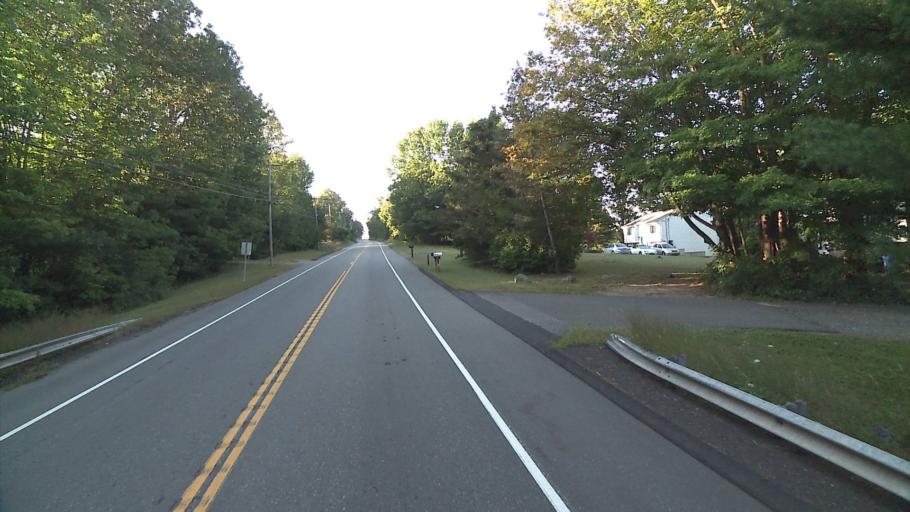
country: US
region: Connecticut
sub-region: Tolland County
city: South Coventry
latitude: 41.8192
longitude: -72.3102
